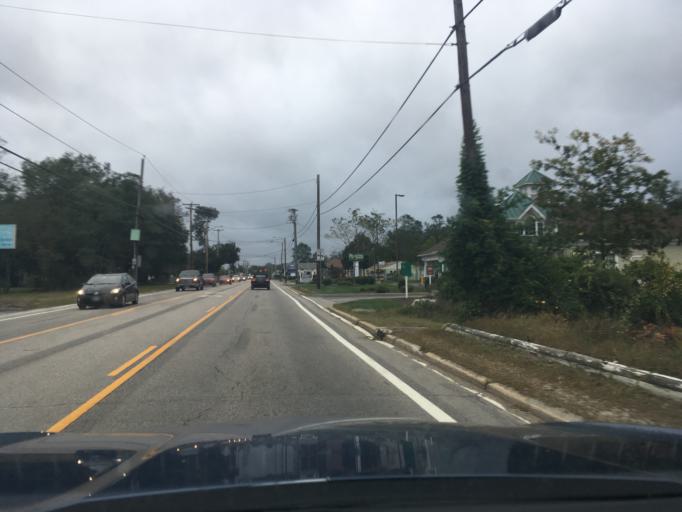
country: US
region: Rhode Island
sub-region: Washington County
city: North Kingstown
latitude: 41.5936
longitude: -71.4564
